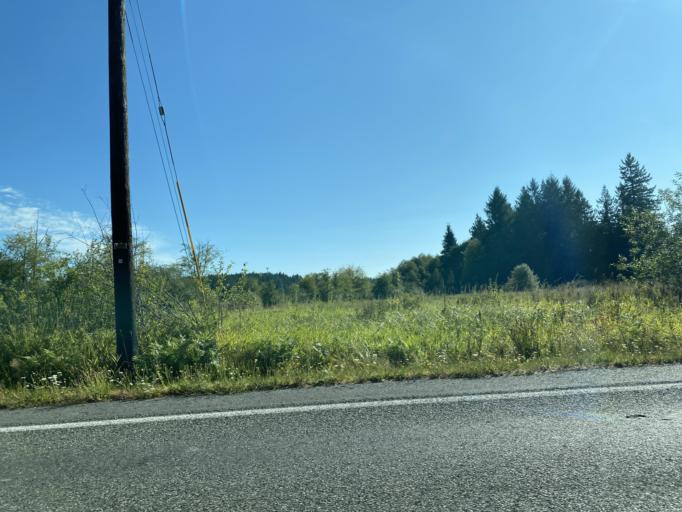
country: US
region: Washington
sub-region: Thurston County
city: Tanglewilde-Thompson Place
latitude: 46.9630
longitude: -122.7630
